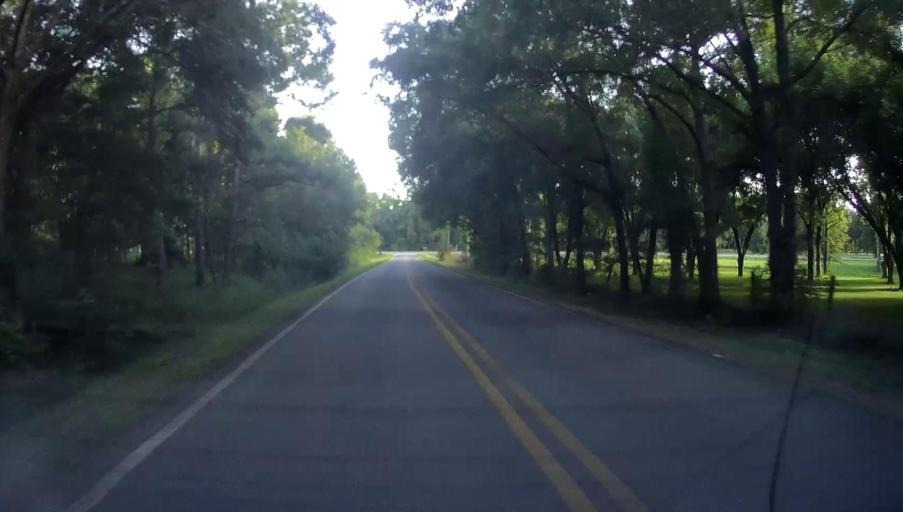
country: US
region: Georgia
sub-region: Pulaski County
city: Hawkinsville
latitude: 32.2697
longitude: -83.5381
